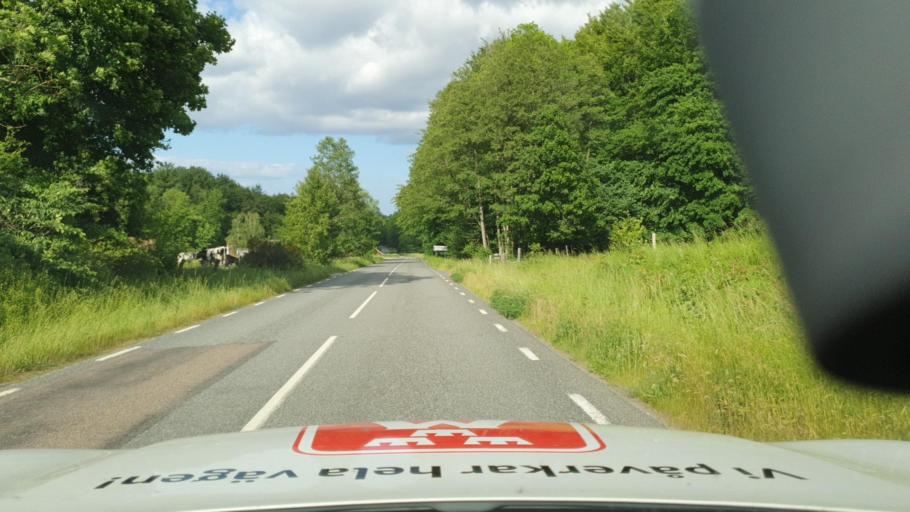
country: SE
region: Skane
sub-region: Simrishamns Kommun
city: Kivik
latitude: 55.6173
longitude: 14.2370
